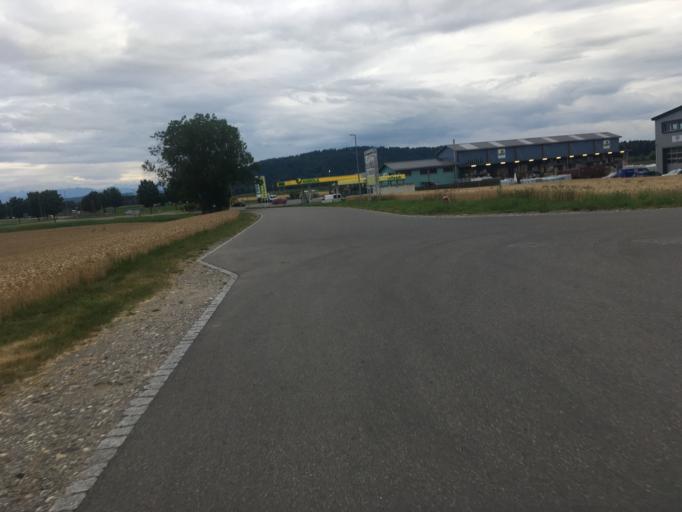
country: CH
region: Bern
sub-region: Seeland District
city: Ins
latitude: 46.9973
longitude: 7.1083
